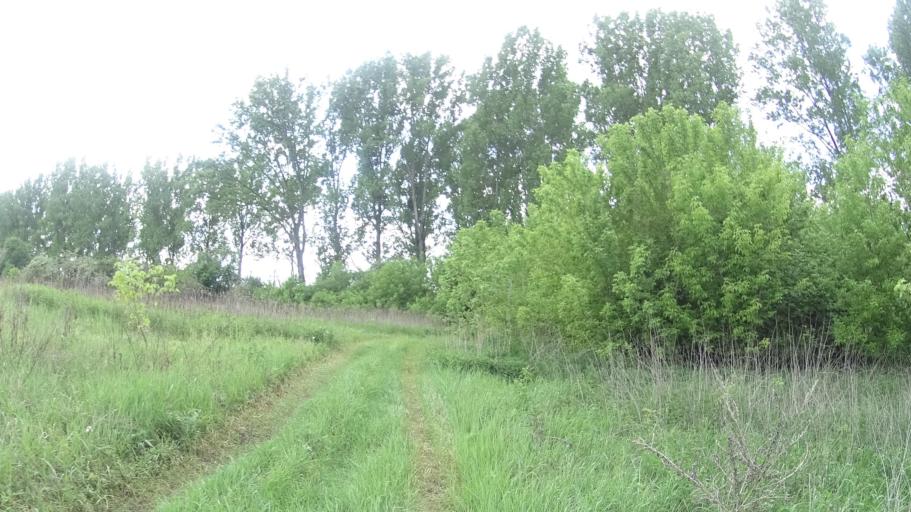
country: HU
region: Komarom-Esztergom
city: Dorog
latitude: 47.7123
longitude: 18.7555
